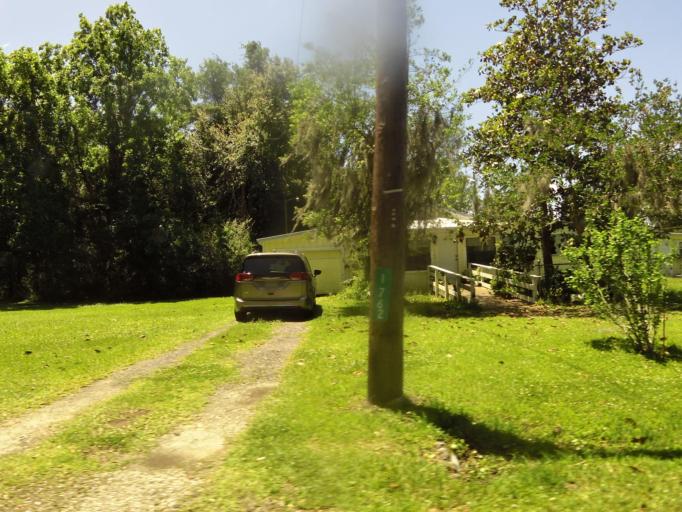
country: US
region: Florida
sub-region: Bradford County
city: Starke
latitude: 30.0475
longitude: -82.0736
